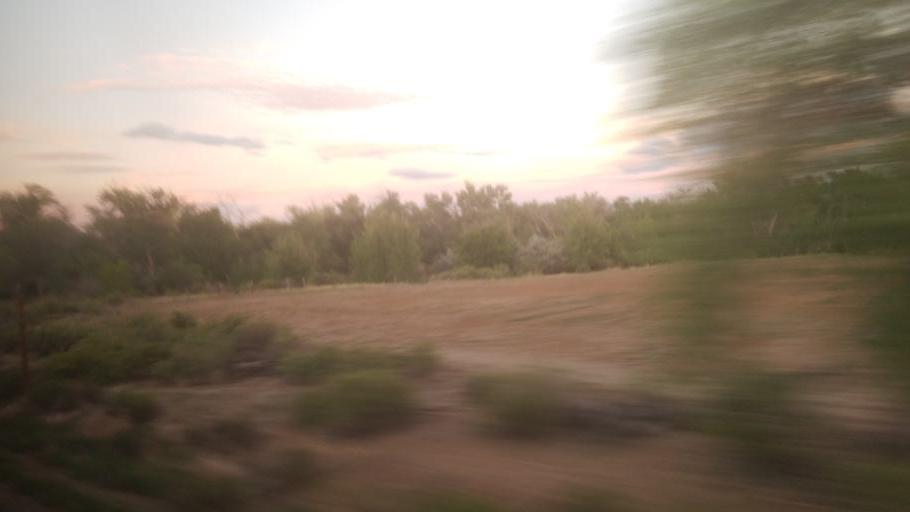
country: US
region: Colorado
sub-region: Las Animas County
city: Trinidad
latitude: 37.2402
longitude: -104.4275
